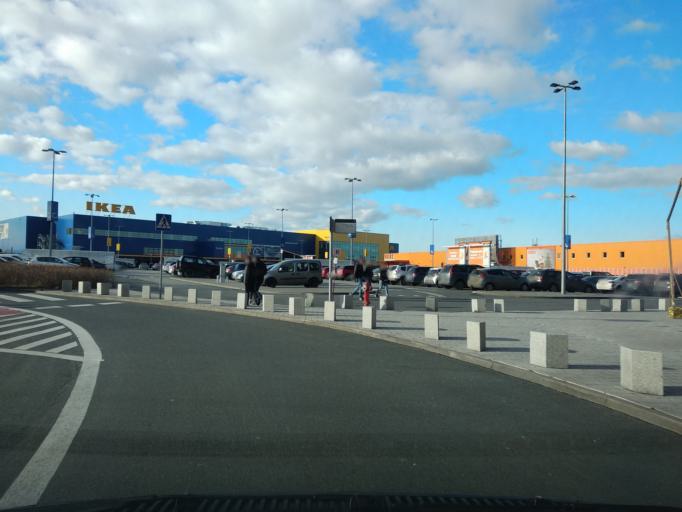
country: PL
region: Lower Silesian Voivodeship
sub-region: Powiat wroclawski
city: Bielany Wroclawskie
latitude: 51.0482
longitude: 16.9588
